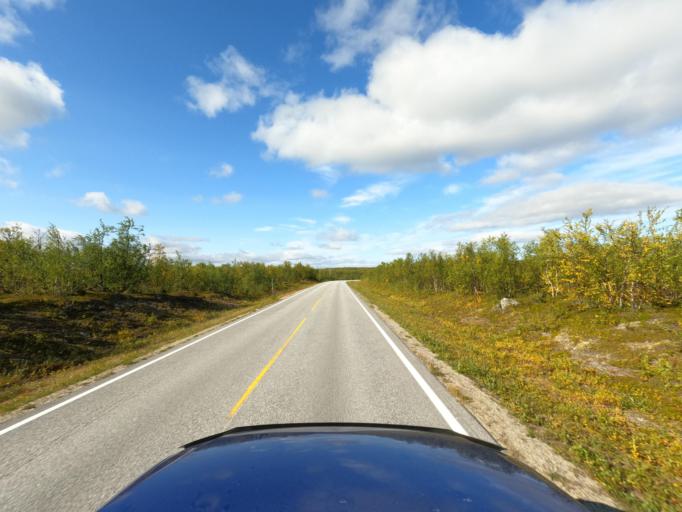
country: NO
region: Finnmark Fylke
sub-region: Karasjok
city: Karasjohka
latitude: 69.6098
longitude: 25.3130
